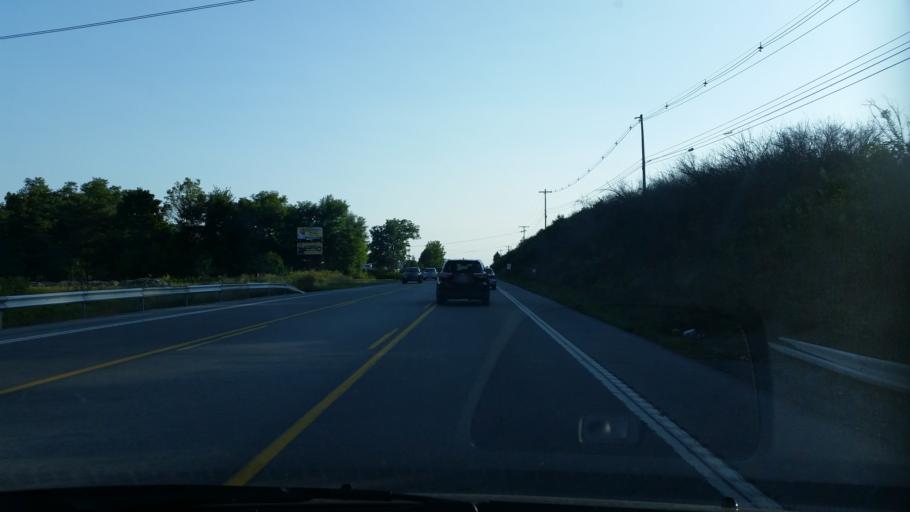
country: US
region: Pennsylvania
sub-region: Blair County
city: Bellwood
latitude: 40.5764
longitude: -78.3310
